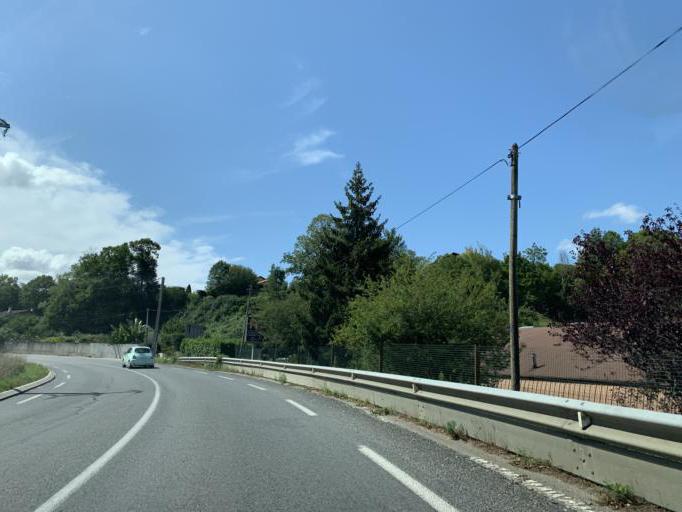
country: FR
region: Rhone-Alpes
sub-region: Departement du Rhone
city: Jons
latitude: 45.8096
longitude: 5.0832
